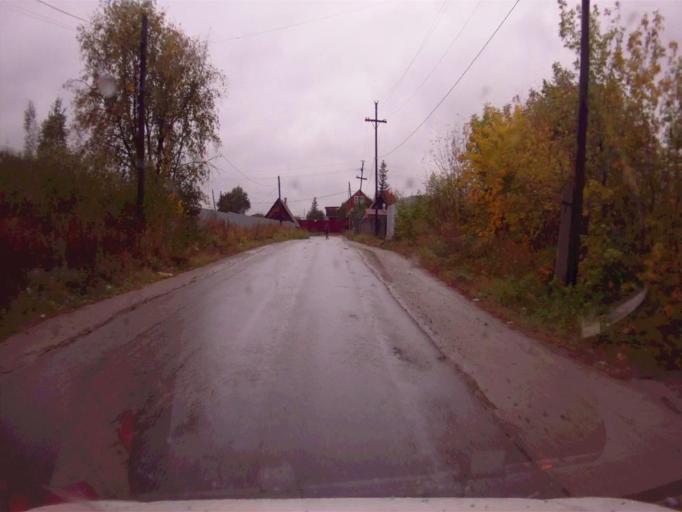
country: RU
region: Chelyabinsk
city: Kyshtym
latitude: 55.7142
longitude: 60.5570
